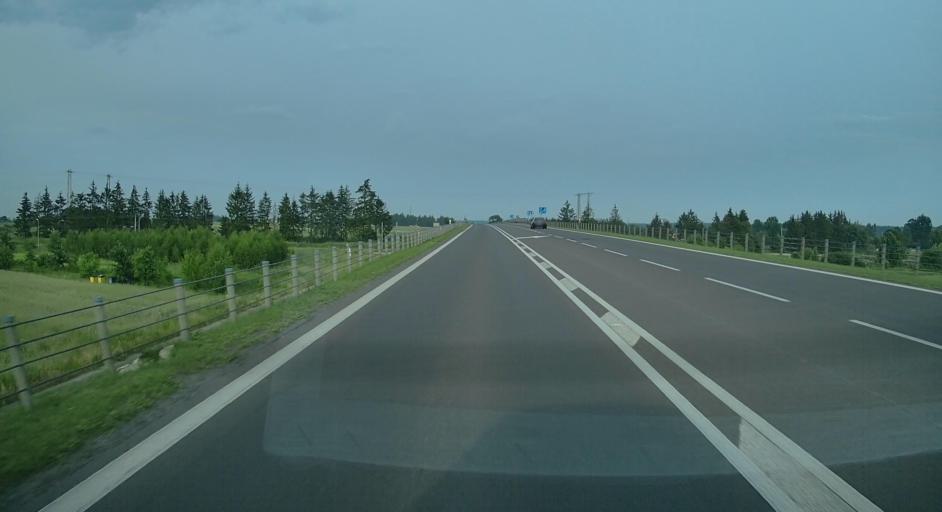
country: PL
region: Masovian Voivodeship
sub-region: Siedlce
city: Siedlce
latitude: 52.1318
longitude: 22.3043
